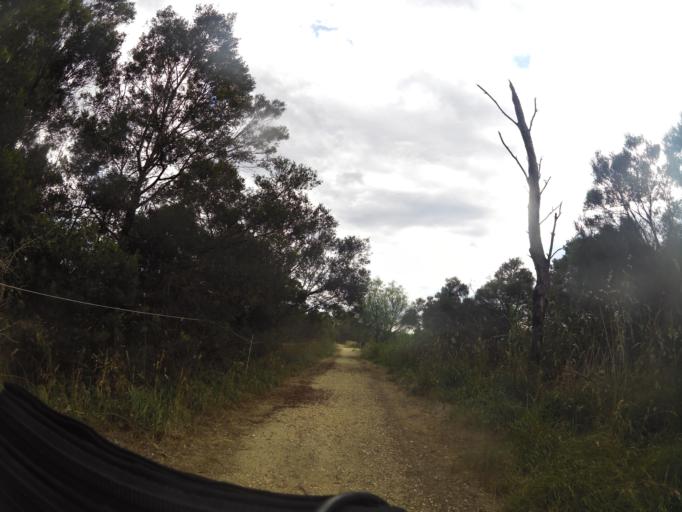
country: AU
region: Victoria
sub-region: Latrobe
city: Traralgon
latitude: -38.0523
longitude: 146.6287
